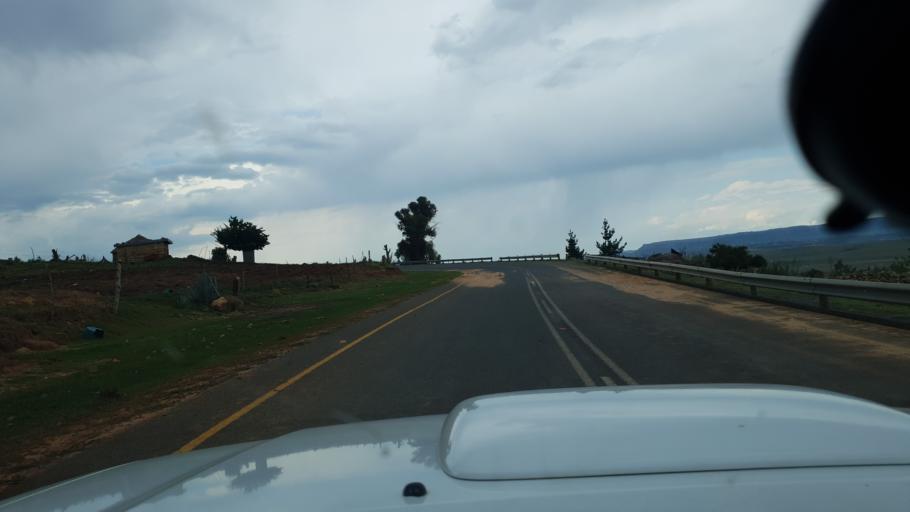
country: LS
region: Maseru
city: Maseru
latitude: -29.4594
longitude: 27.4906
